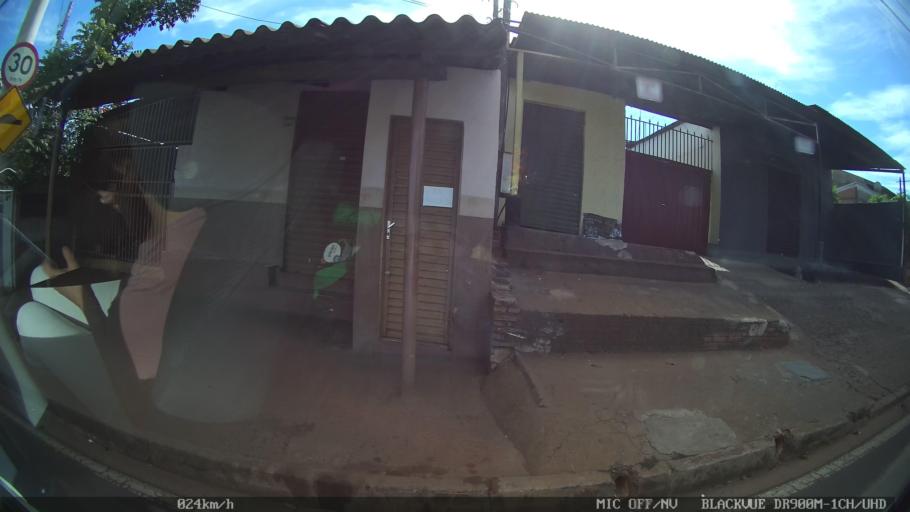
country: BR
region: Sao Paulo
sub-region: Sao Jose Do Rio Preto
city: Sao Jose do Rio Preto
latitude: -20.8418
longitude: -49.3345
